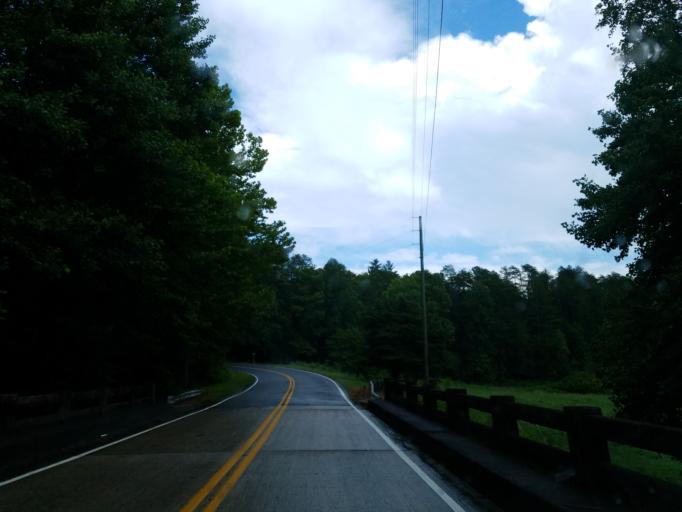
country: US
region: Georgia
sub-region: Gilmer County
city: Ellijay
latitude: 34.6749
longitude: -84.3372
